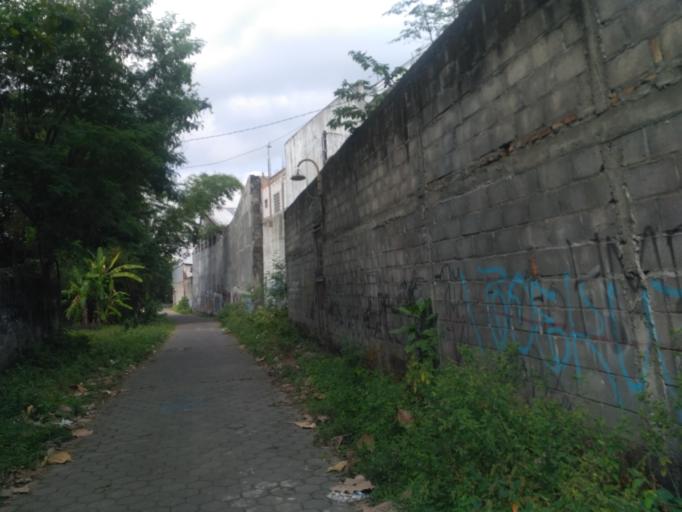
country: ID
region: Daerah Istimewa Yogyakarta
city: Melati
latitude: -7.7563
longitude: 110.3641
